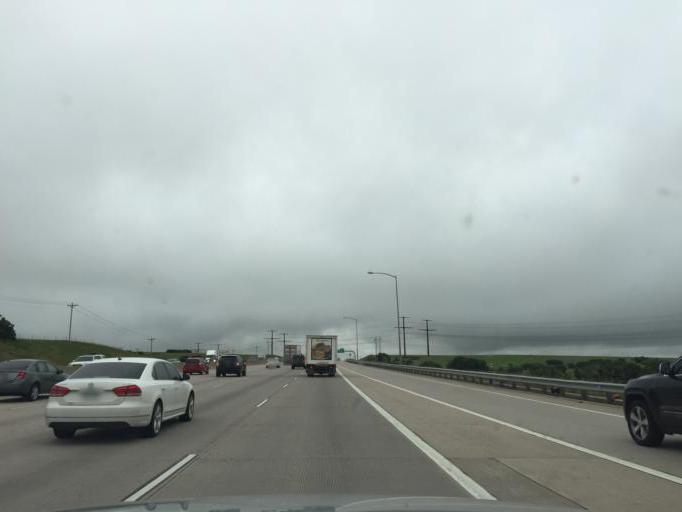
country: US
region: Colorado
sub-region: Douglas County
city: Castle Pines
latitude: 39.4536
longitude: -104.8752
